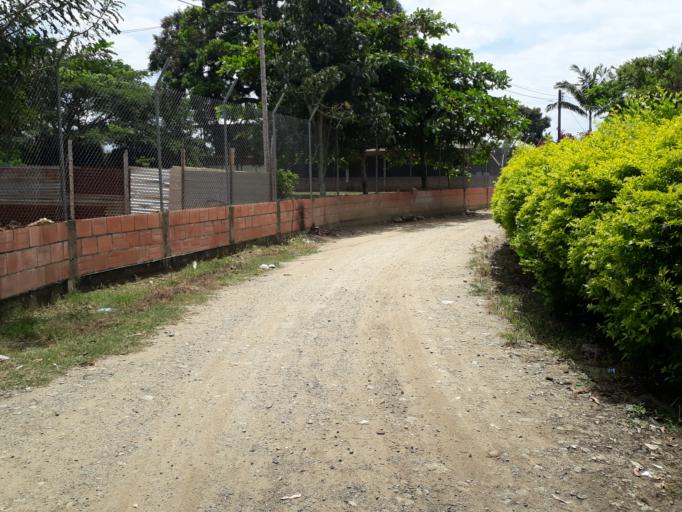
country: CO
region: Valle del Cauca
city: Cali
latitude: 3.3597
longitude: -76.4839
